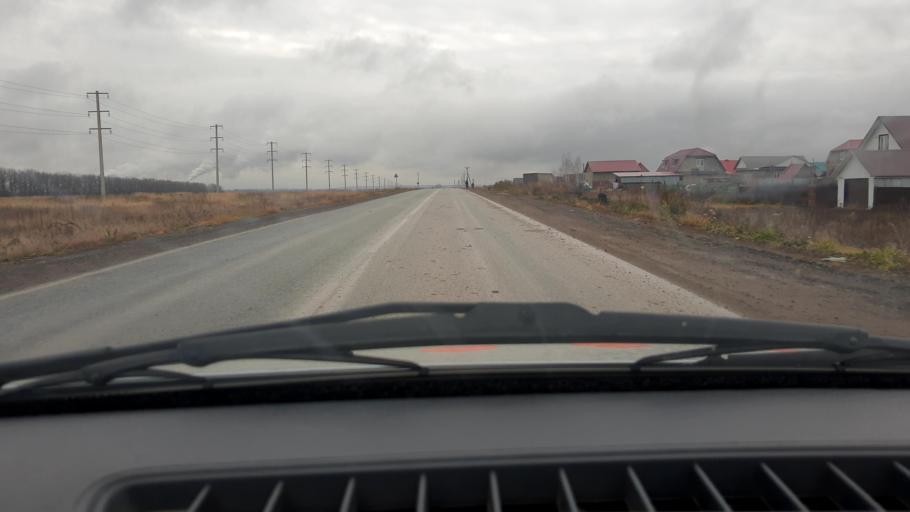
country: RU
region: Bashkortostan
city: Iglino
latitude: 54.7941
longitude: 56.2514
